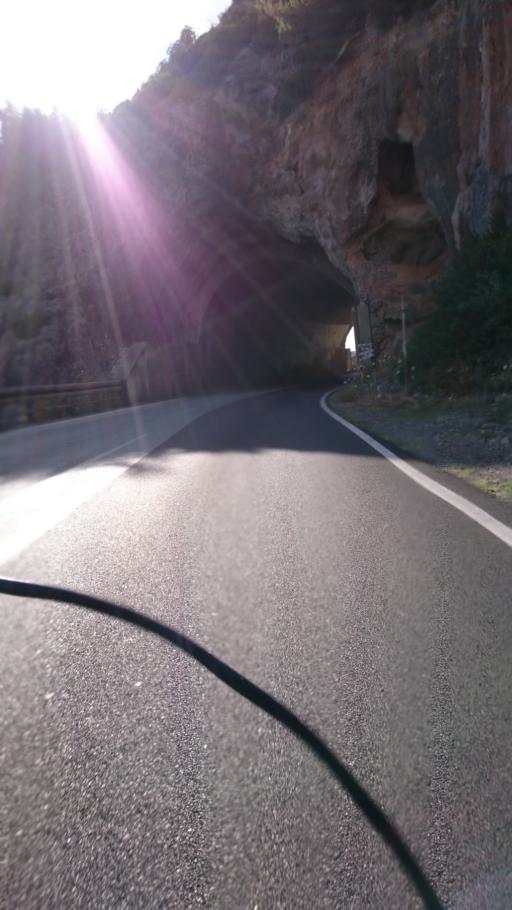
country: IT
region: Campania
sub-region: Provincia di Salerno
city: Marina di Camerota
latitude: 40.0098
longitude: 15.3381
